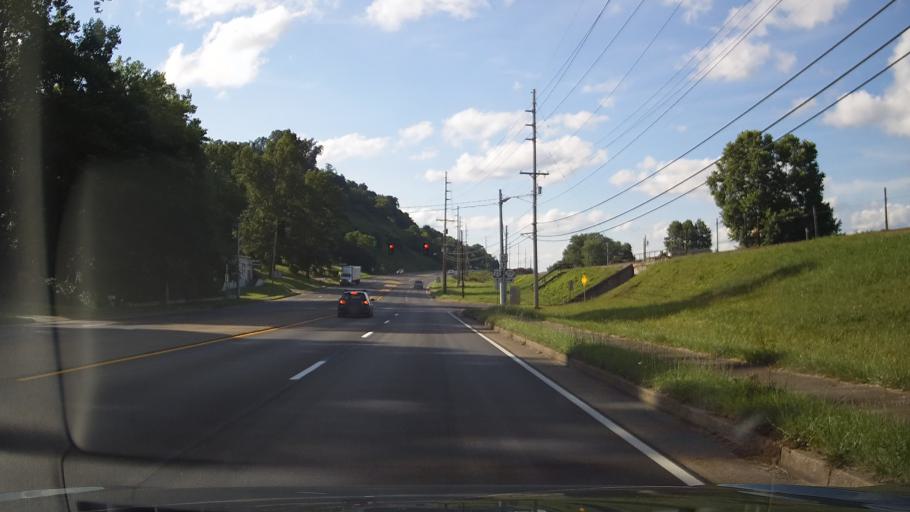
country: US
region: Kentucky
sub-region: Boyd County
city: Catlettsburg
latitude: 38.4190
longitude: -82.6004
